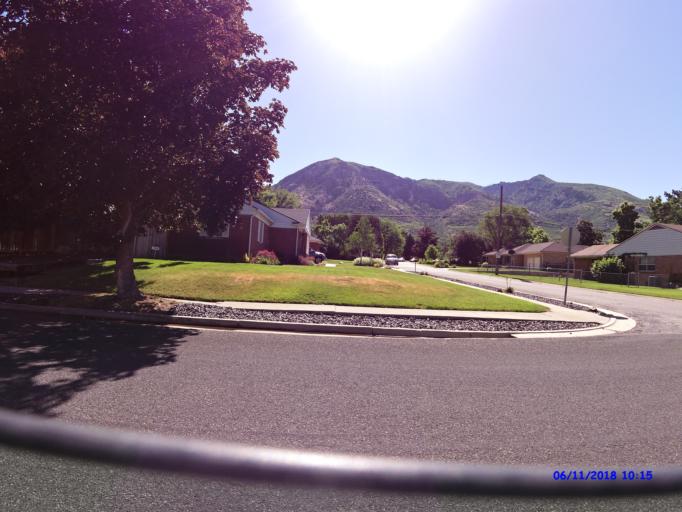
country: US
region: Utah
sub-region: Weber County
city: South Ogden
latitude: 41.2079
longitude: -111.9453
